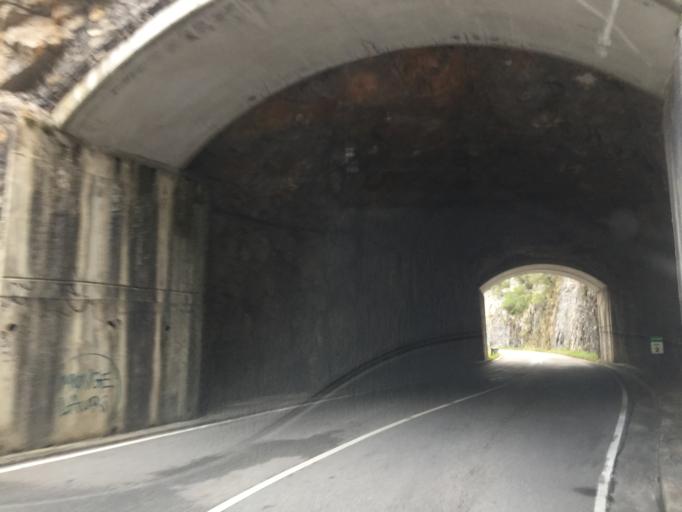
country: ES
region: Asturias
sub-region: Province of Asturias
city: Carrena
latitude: 43.2903
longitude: -4.8256
